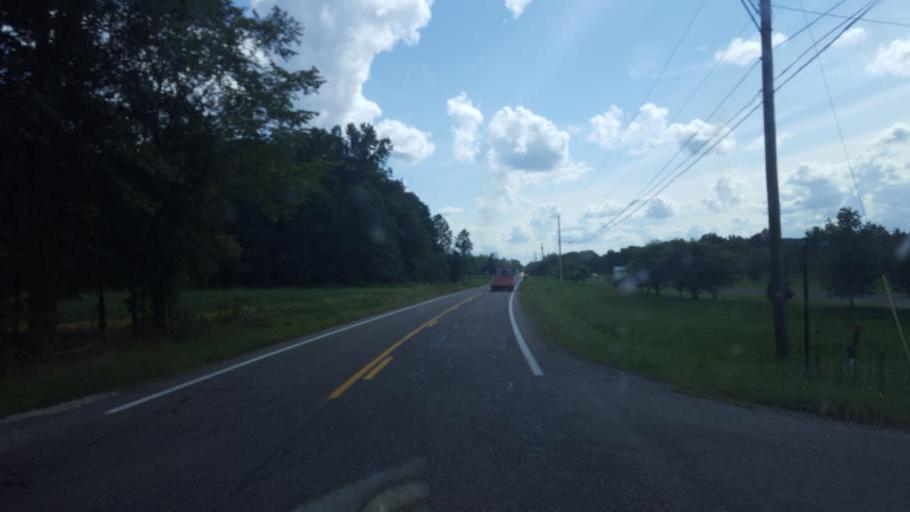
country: US
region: Ohio
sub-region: Portage County
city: Hiram
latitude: 41.2585
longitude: -81.1454
